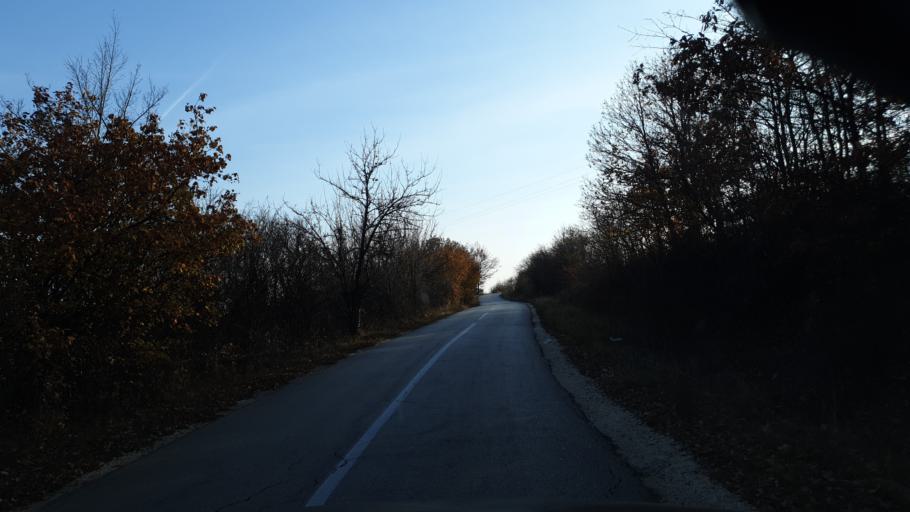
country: RS
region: Central Serbia
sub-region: Borski Okrug
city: Bor
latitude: 44.0503
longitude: 22.0949
